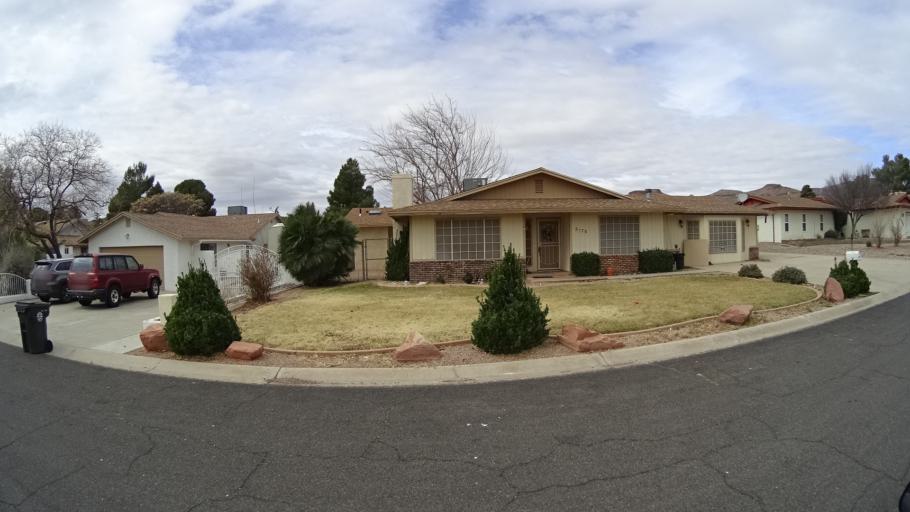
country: US
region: Arizona
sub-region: Mohave County
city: New Kingman-Butler
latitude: 35.2355
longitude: -114.0431
